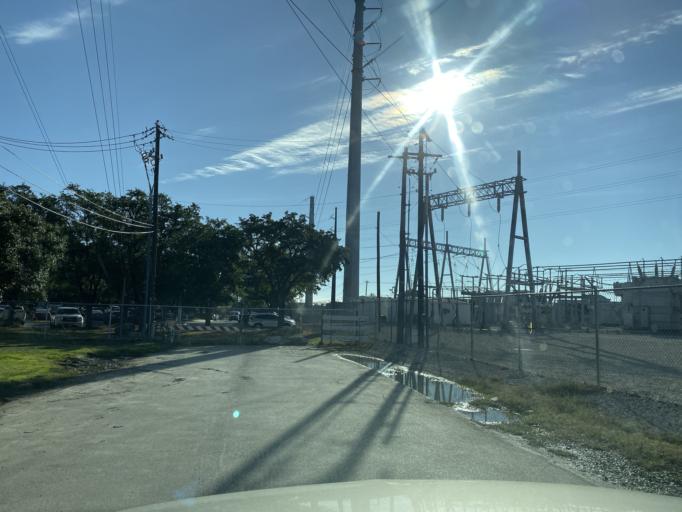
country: US
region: Texas
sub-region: Williamson County
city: Jollyville
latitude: 30.4014
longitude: -97.7443
